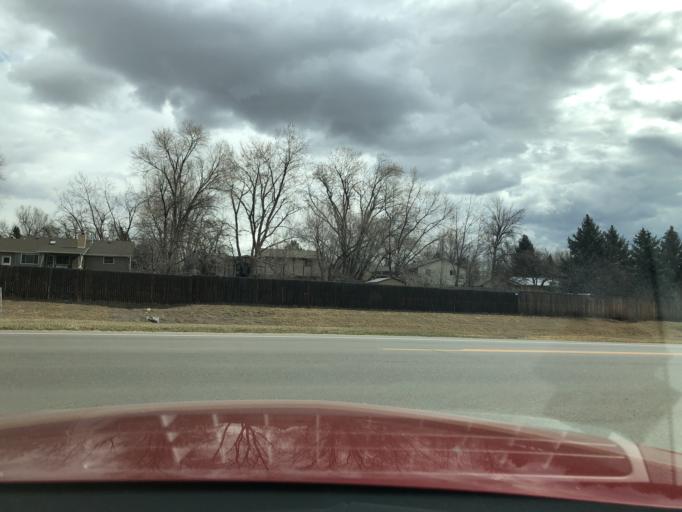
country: US
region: Colorado
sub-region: Boulder County
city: Gunbarrel
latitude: 40.0590
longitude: -105.1785
